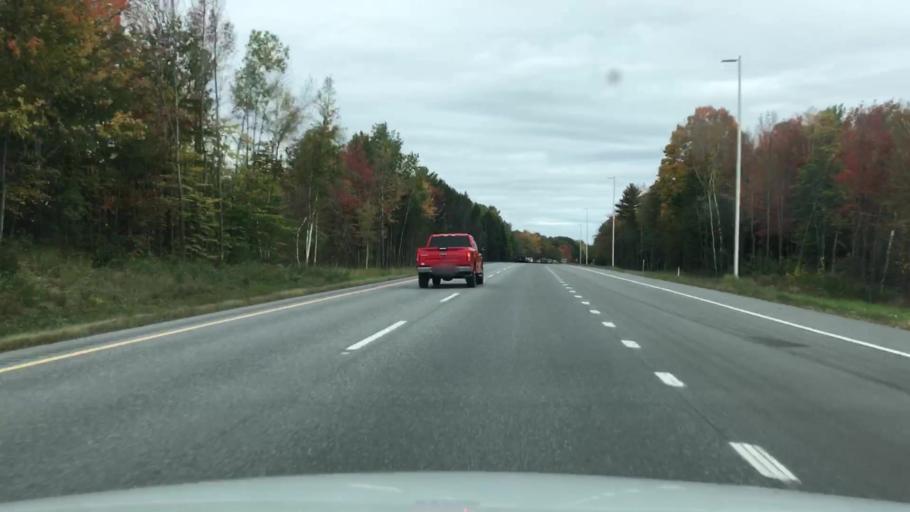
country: US
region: Maine
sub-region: Kennebec County
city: Oakland
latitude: 44.5095
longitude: -69.7026
